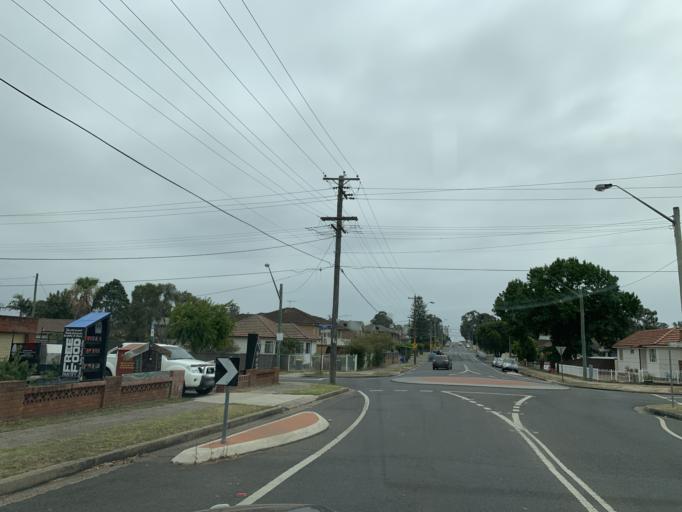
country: AU
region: New South Wales
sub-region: Blacktown
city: Doonside
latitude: -33.7602
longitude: 150.8700
